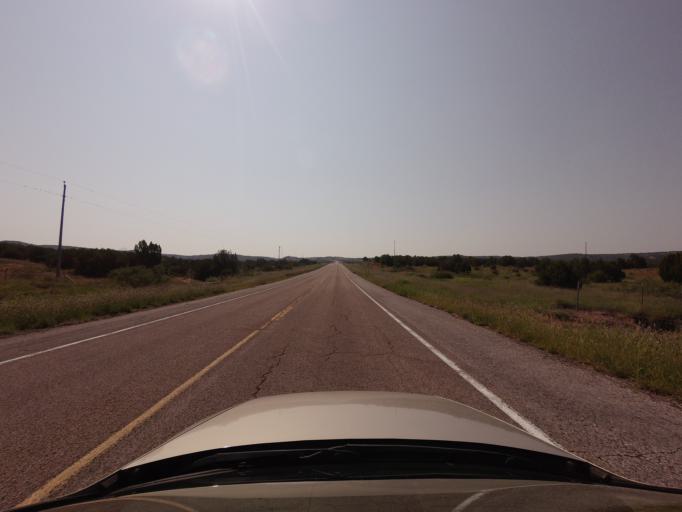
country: US
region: New Mexico
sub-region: Quay County
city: Tucumcari
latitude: 34.8351
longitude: -103.7572
